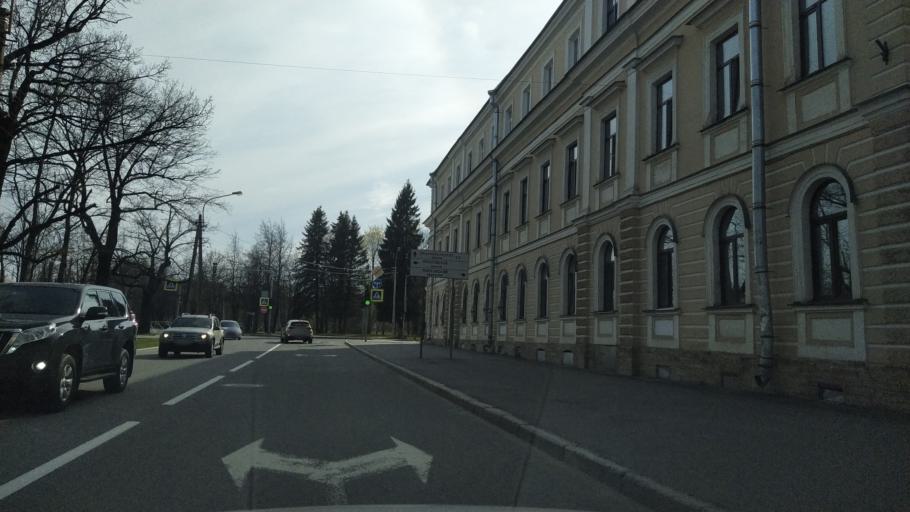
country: RU
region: St.-Petersburg
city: Pushkin
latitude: 59.7168
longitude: 30.4205
